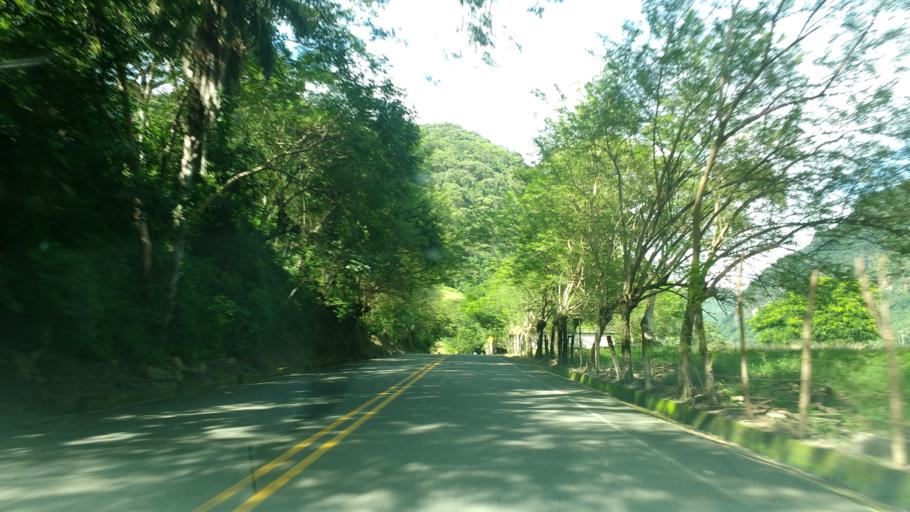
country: CO
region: Antioquia
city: Concordia
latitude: 6.0787
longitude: -75.8608
